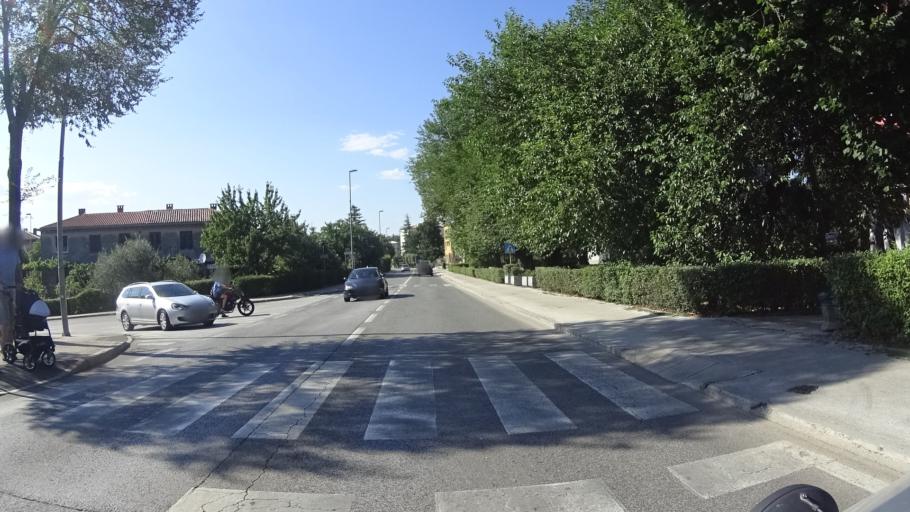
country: HR
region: Istarska
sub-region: Grad Labin
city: Labin
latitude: 45.0925
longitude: 14.1232
